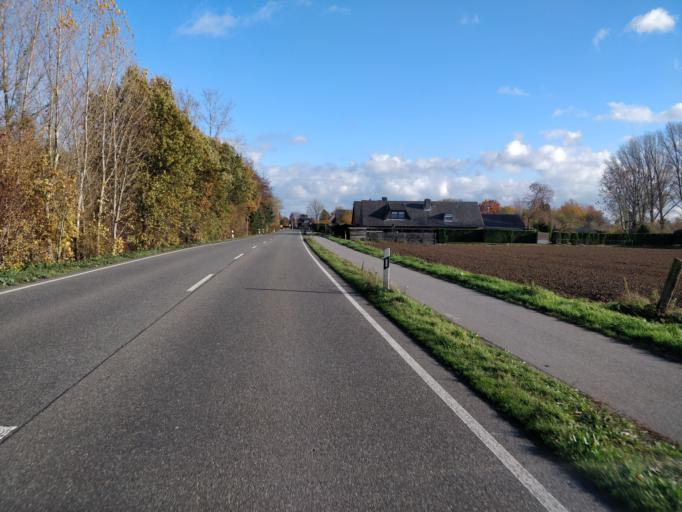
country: DE
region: North Rhine-Westphalia
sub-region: Regierungsbezirk Dusseldorf
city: Emmerich
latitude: 51.8276
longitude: 6.2944
